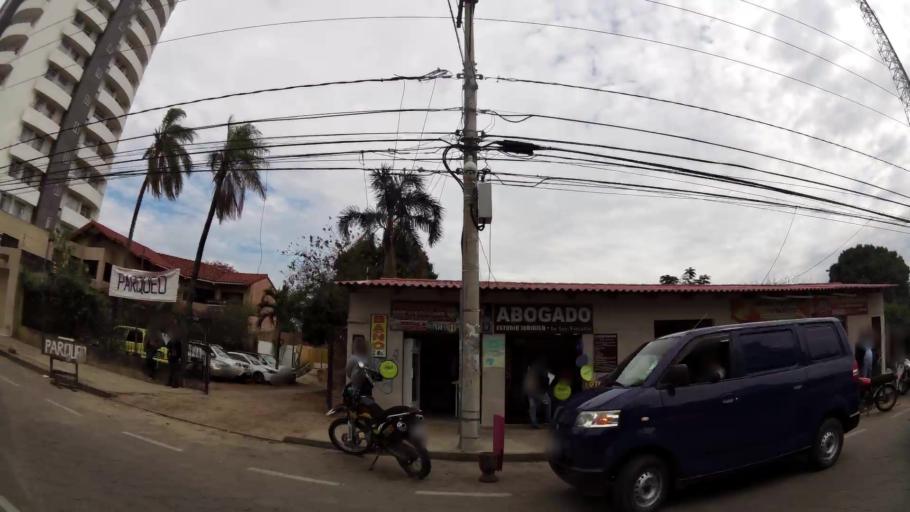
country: BO
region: Santa Cruz
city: Santa Cruz de la Sierra
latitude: -17.7662
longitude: -63.1879
